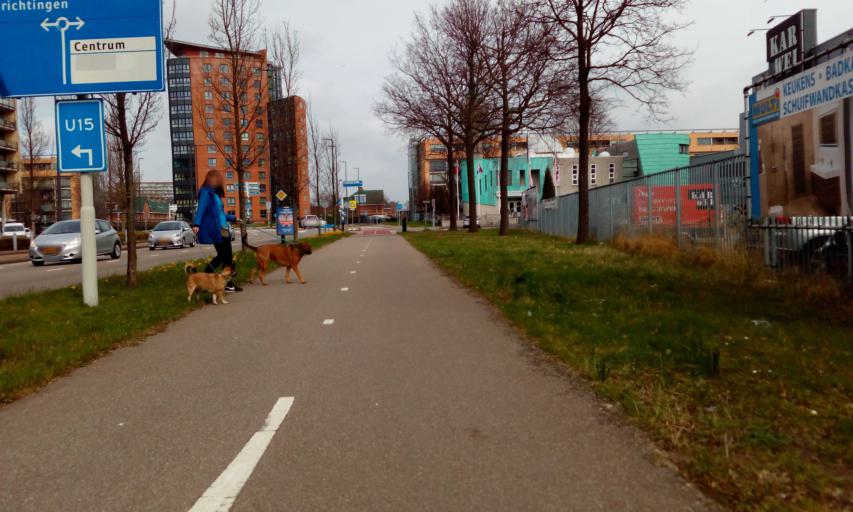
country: NL
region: South Holland
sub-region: Gemeente Maassluis
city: Maassluis
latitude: 51.9260
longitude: 4.2453
